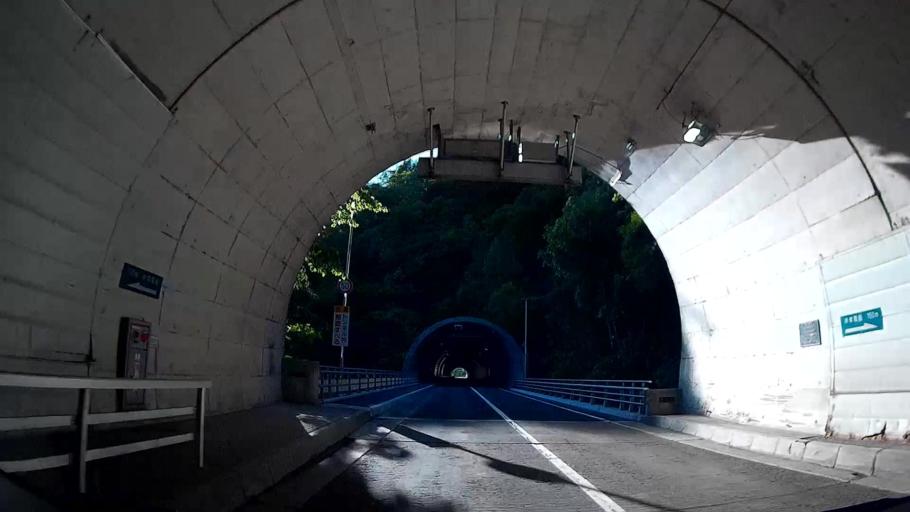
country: JP
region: Hokkaido
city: Sapporo
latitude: 42.9956
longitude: 141.1578
